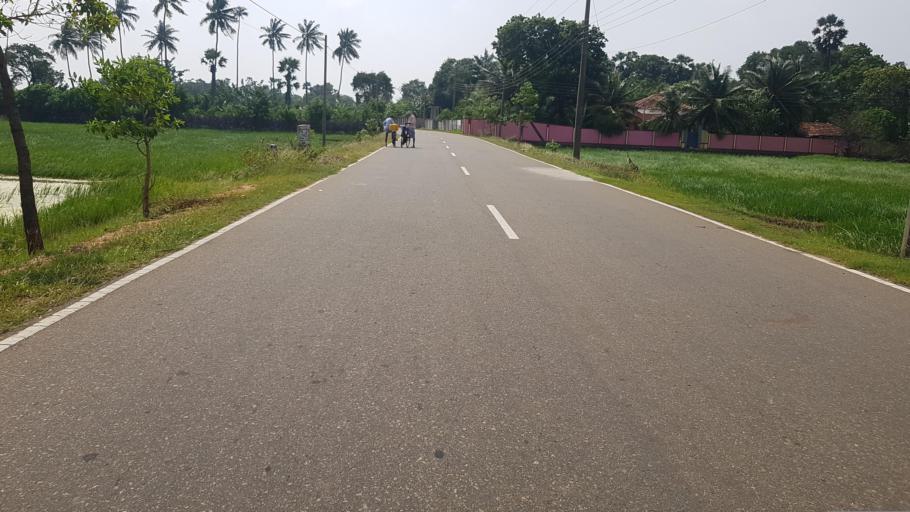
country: LK
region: Northern Province
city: Jaffna
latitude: 9.7259
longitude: 79.9476
